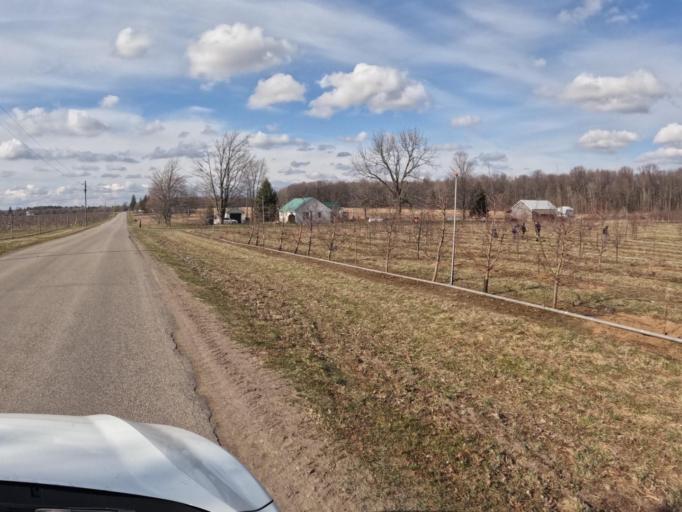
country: CA
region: Ontario
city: Norfolk County
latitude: 42.8777
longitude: -80.2807
